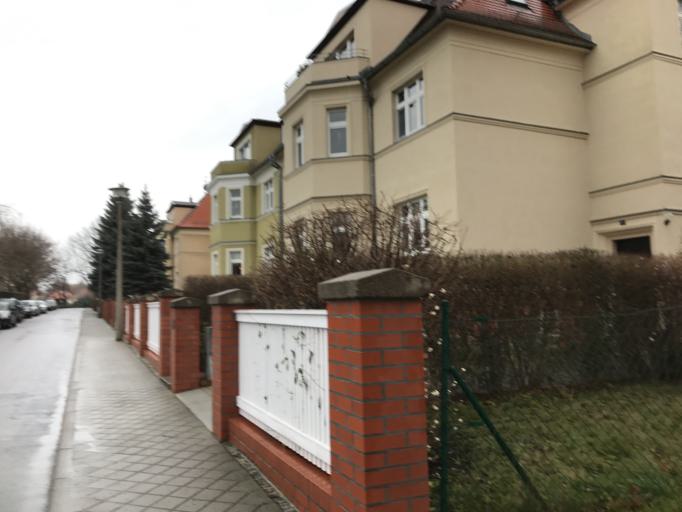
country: DE
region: Saxony
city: Goerlitz
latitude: 51.1419
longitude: 14.9645
